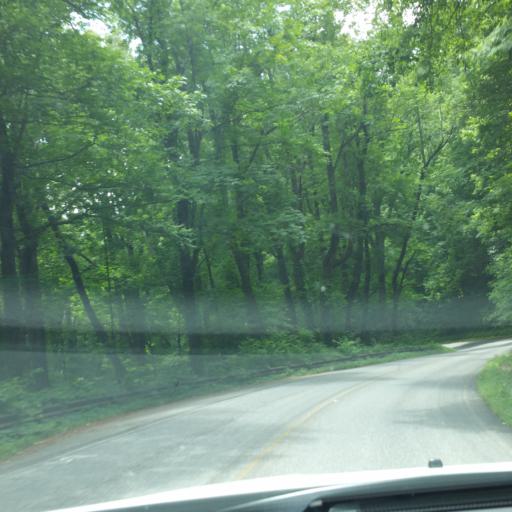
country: US
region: North Carolina
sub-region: Transylvania County
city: Brevard
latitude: 35.3661
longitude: -82.7820
